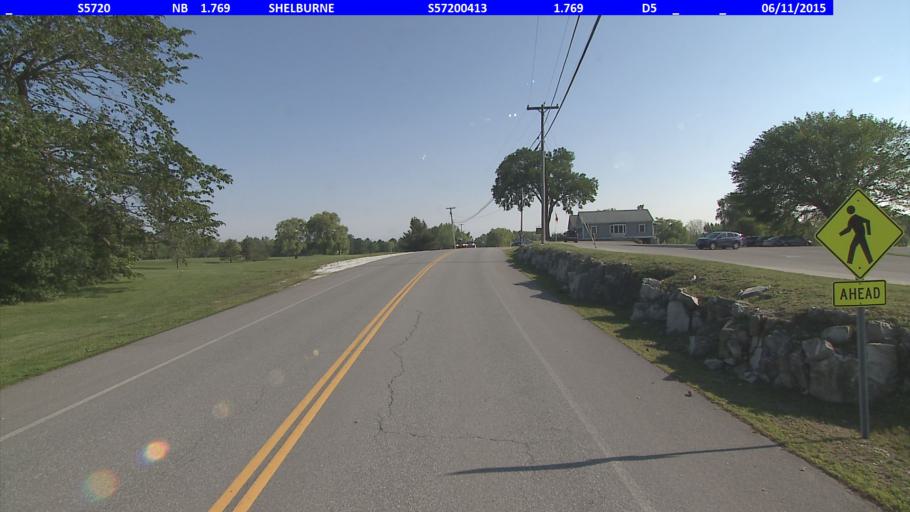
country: US
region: Vermont
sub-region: Chittenden County
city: South Burlington
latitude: 44.3933
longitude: -73.2011
